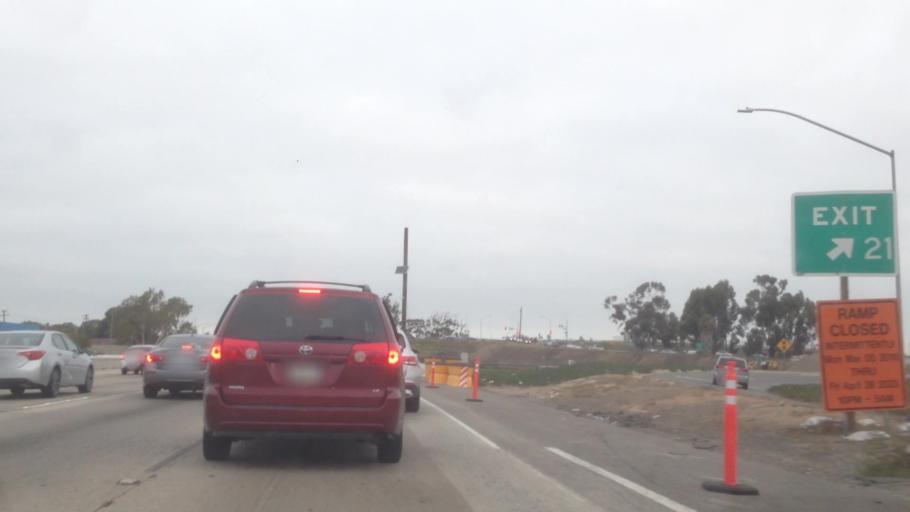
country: US
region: California
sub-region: Orange County
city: Westminster
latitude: 33.7707
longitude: -118.0357
